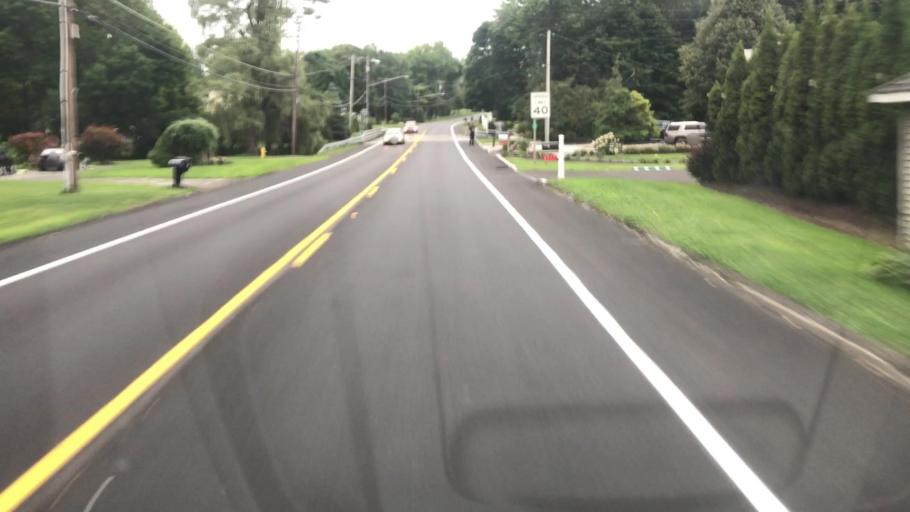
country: US
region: New York
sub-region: Cayuga County
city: Melrose Park
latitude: 42.9017
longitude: -76.5281
